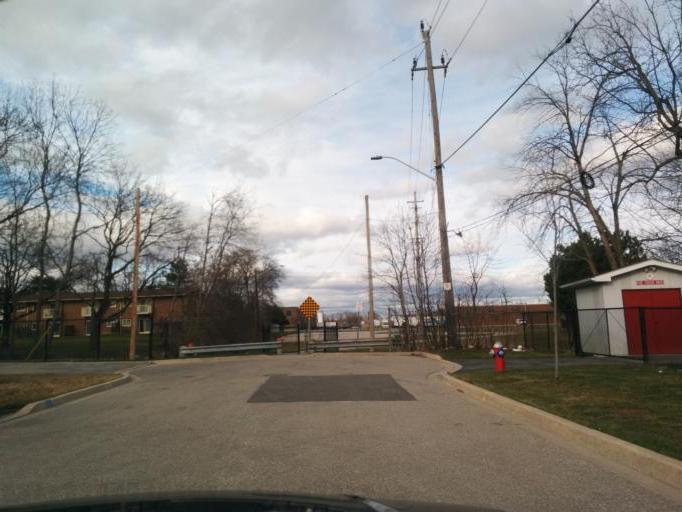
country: CA
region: Ontario
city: Etobicoke
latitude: 43.5706
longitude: -79.5640
